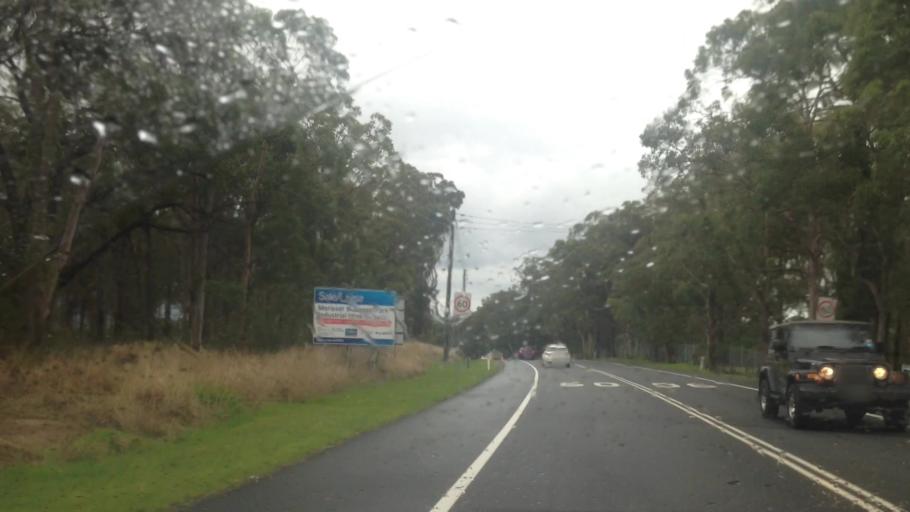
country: AU
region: New South Wales
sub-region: Lake Macquarie Shire
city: Dora Creek
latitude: -33.1193
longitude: 151.4779
